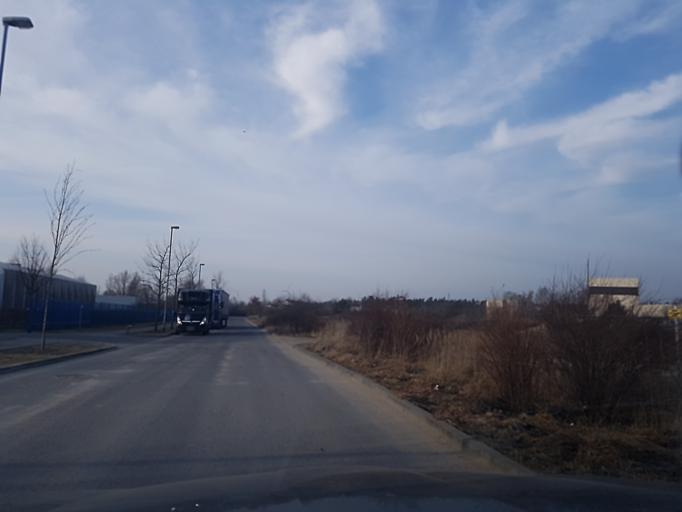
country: DE
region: Brandenburg
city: Finsterwalde
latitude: 51.6328
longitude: 13.7435
